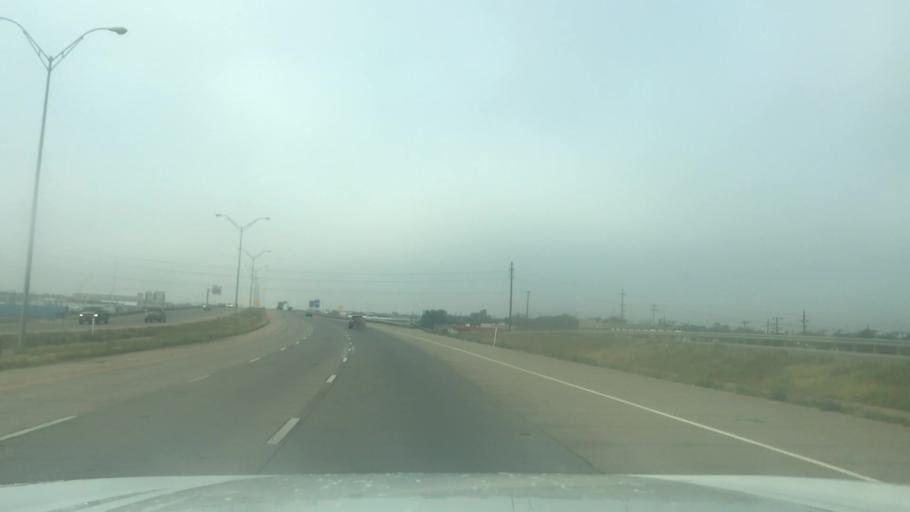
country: US
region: Texas
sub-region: Lubbock County
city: Lubbock
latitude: 33.5690
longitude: -101.8450
